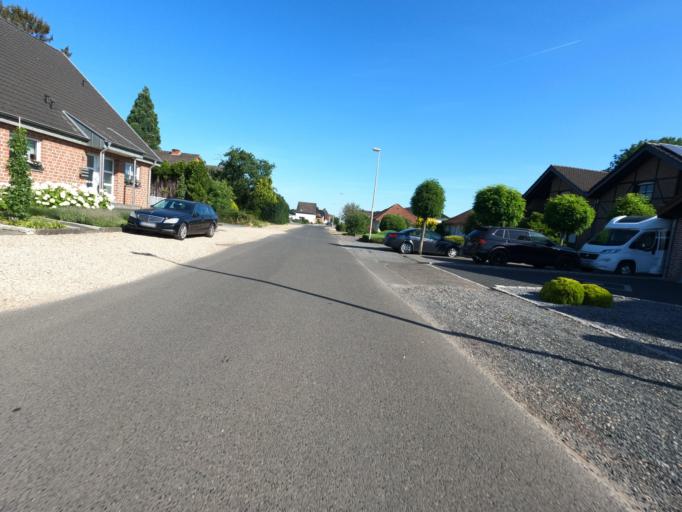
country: DE
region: North Rhine-Westphalia
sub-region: Regierungsbezirk Koln
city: Heinsberg
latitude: 51.0727
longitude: 6.1174
